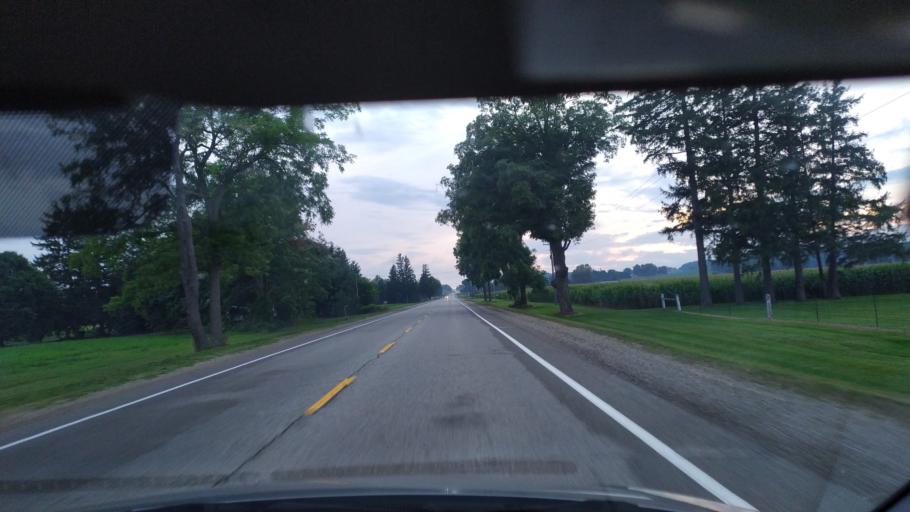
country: CA
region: Ontario
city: Kitchener
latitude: 43.3153
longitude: -80.5452
